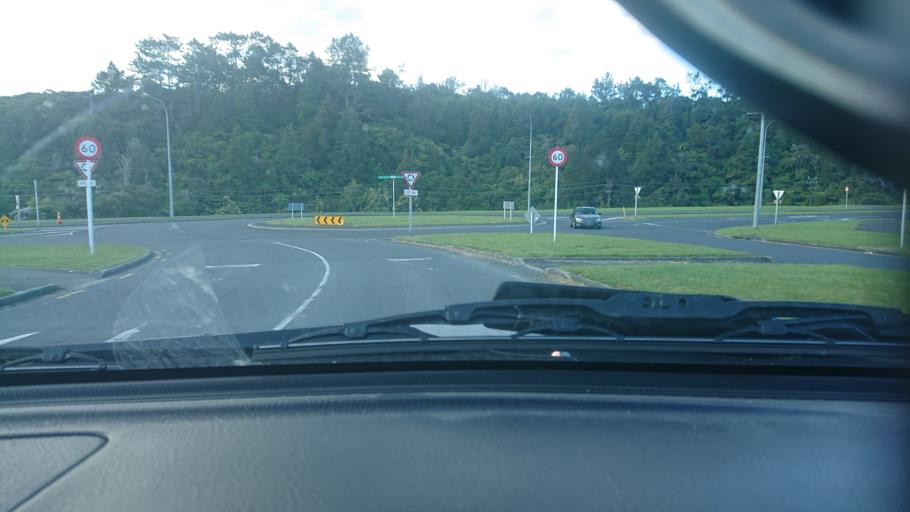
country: NZ
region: Auckland
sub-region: Auckland
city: Rothesay Bay
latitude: -36.7211
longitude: 174.7087
